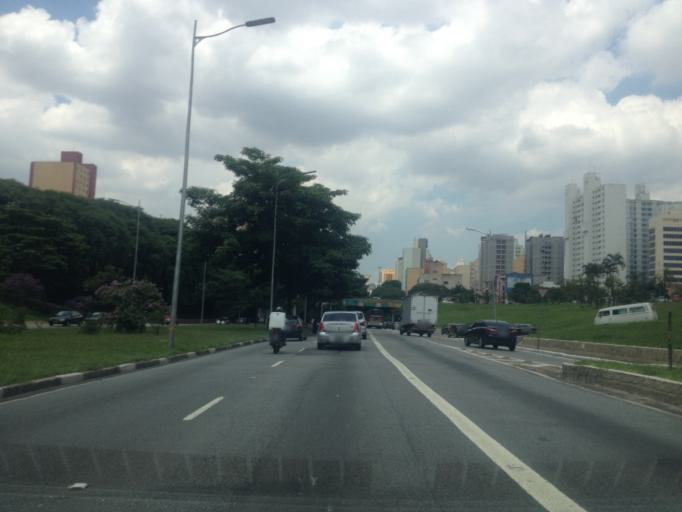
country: BR
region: Sao Paulo
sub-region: Sao Paulo
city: Sao Paulo
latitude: -23.5541
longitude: -46.6369
